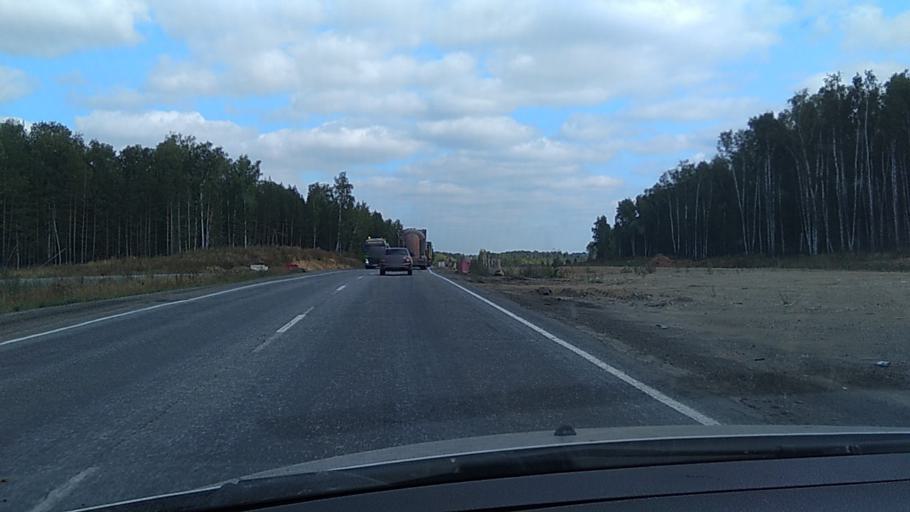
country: RU
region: Chelyabinsk
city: Chebarkul'
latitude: 54.9232
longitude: 60.2821
